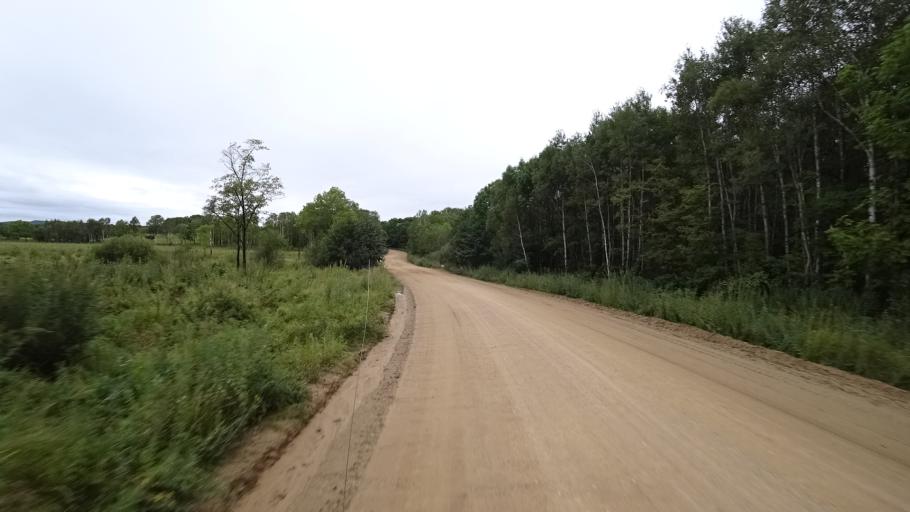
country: RU
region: Primorskiy
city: Rettikhovka
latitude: 44.1809
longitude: 132.8735
